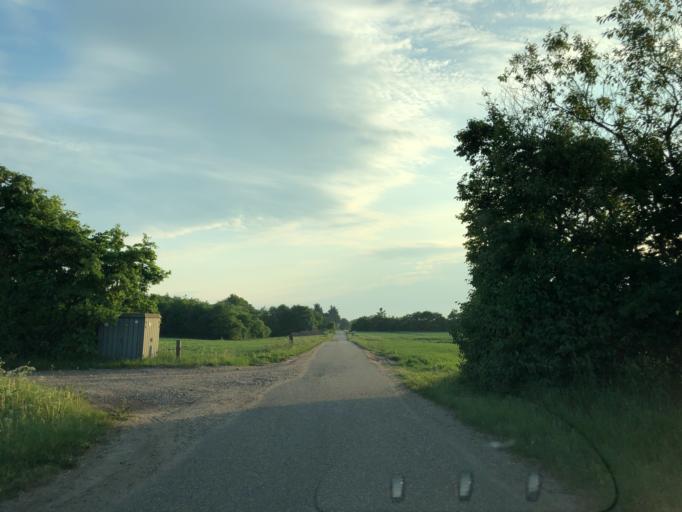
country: DK
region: Central Jutland
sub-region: Holstebro Kommune
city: Holstebro
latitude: 56.3754
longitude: 8.4515
